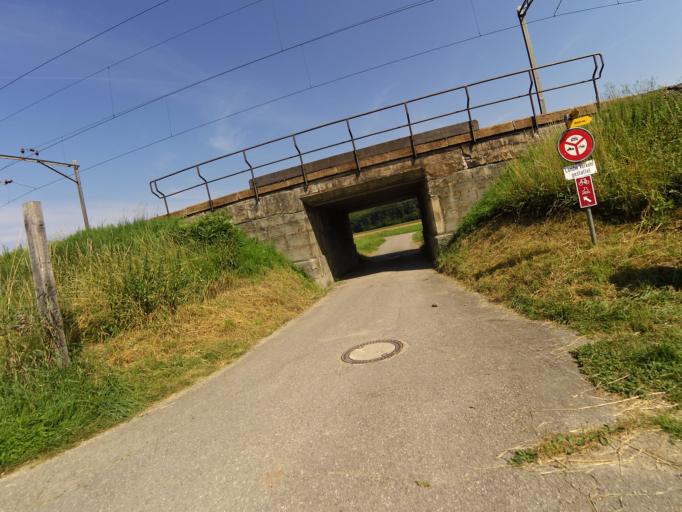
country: CH
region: Thurgau
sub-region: Frauenfeld District
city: Mullheim
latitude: 47.5815
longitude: 9.0036
